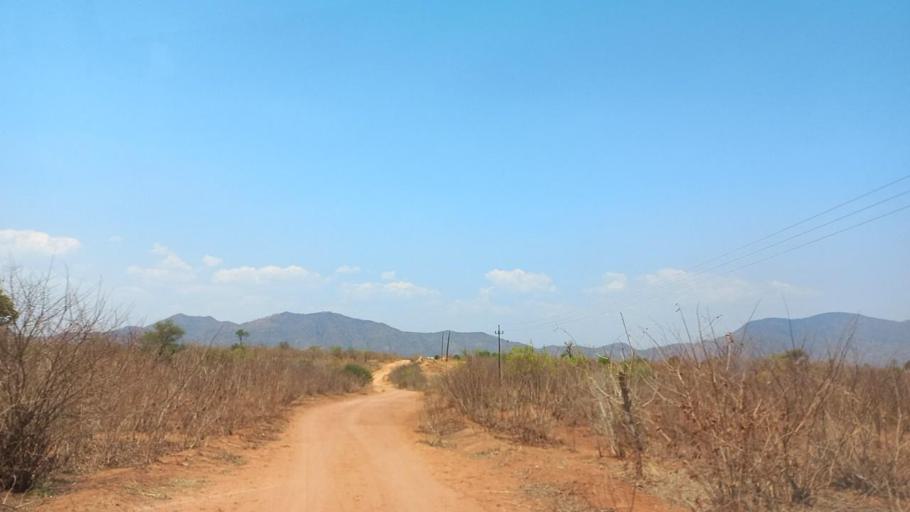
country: ZM
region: Lusaka
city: Luangwa
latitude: -15.5927
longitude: 30.3859
